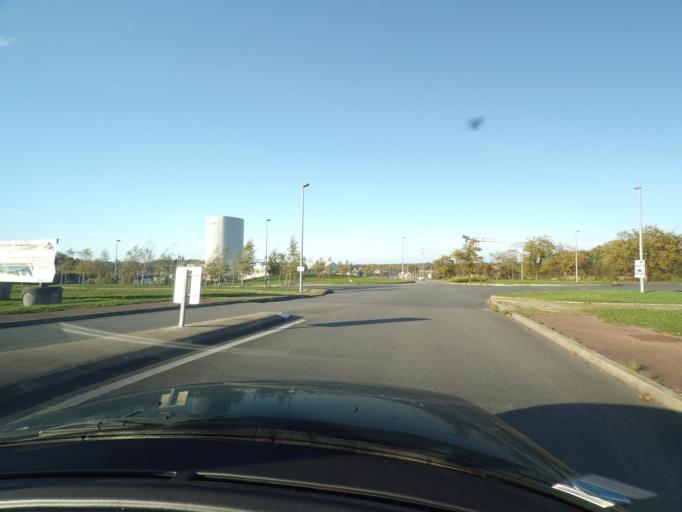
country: FR
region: Pays de la Loire
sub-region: Departement de la Loire-Atlantique
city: Le Bignon
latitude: 47.0969
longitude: -1.4491
